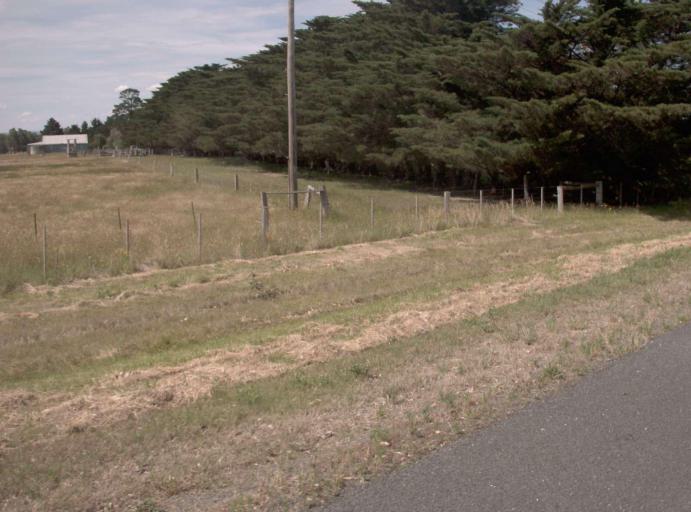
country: AU
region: Victoria
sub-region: East Gippsland
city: Bairnsdale
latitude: -37.8460
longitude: 147.5718
